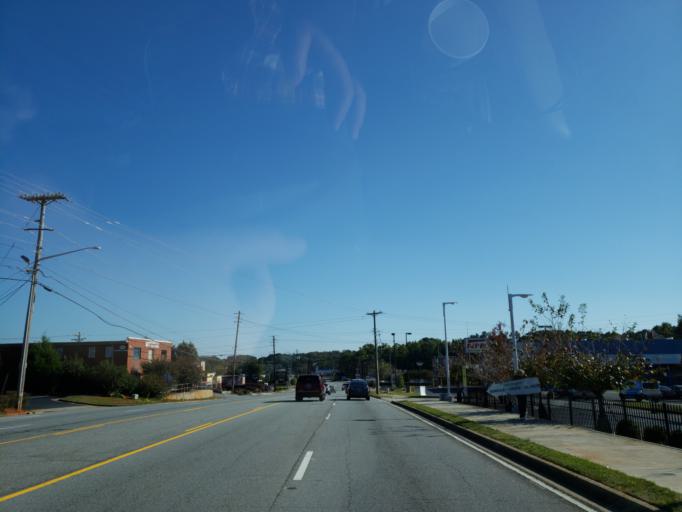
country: US
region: Georgia
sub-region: Gwinnett County
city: Lawrenceville
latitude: 33.9641
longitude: -84.0078
